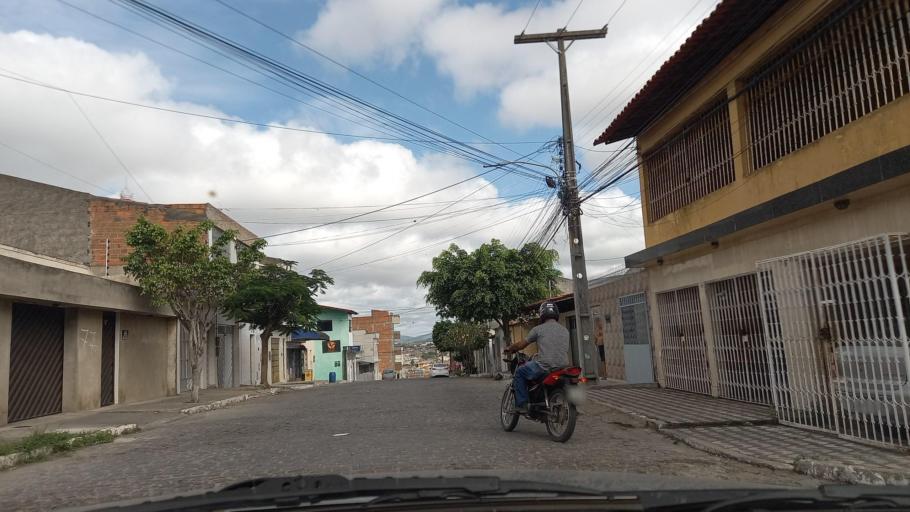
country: BR
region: Pernambuco
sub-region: Caruaru
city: Caruaru
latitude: -8.2853
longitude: -35.9811
